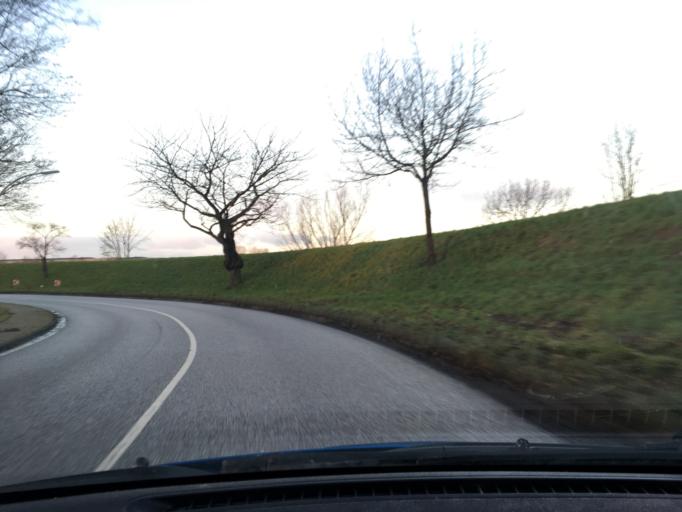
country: DE
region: Hamburg
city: Altona
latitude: 53.5090
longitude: 9.8752
